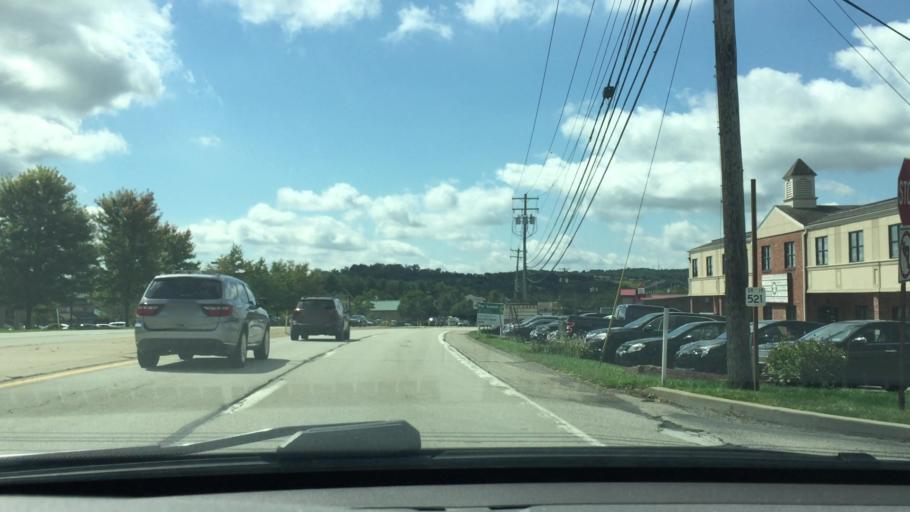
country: US
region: Pennsylvania
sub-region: Washington County
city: Thompsonville
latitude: 40.2643
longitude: -80.1307
